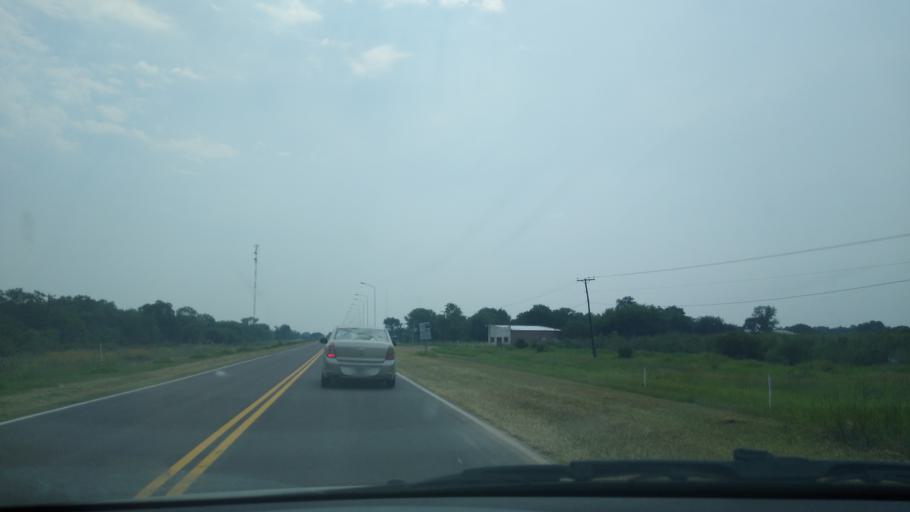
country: AR
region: Chaco
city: La Eduvigis
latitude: -26.8392
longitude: -59.0583
